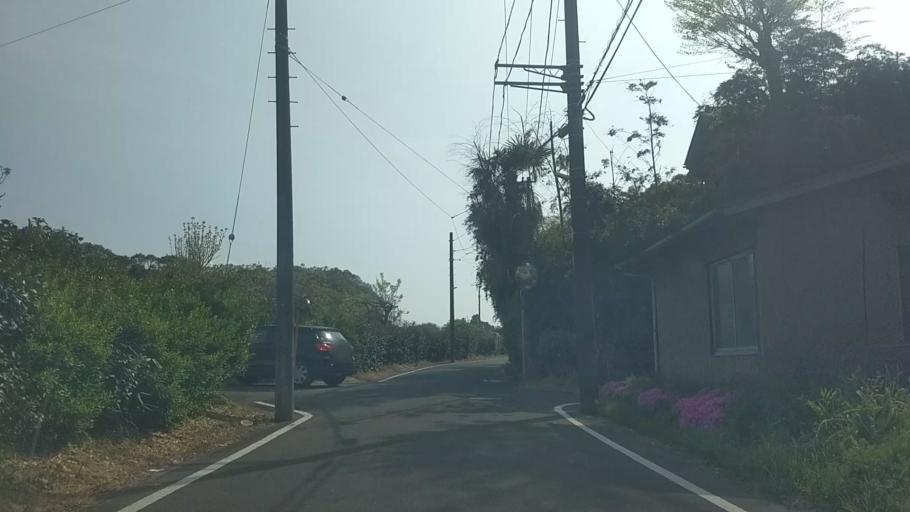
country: JP
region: Kanagawa
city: Kamakura
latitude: 35.3850
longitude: 139.5616
